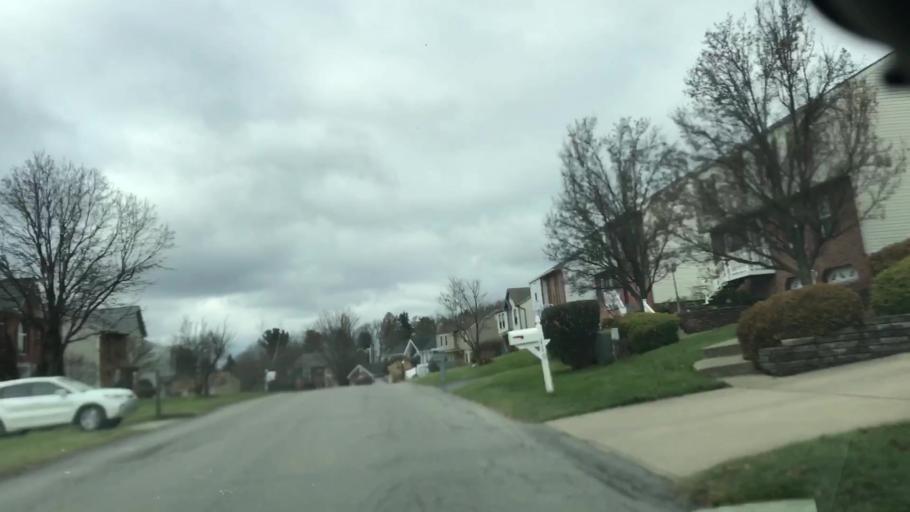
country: US
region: Pennsylvania
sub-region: Allegheny County
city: Enlow
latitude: 40.4524
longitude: -80.2230
